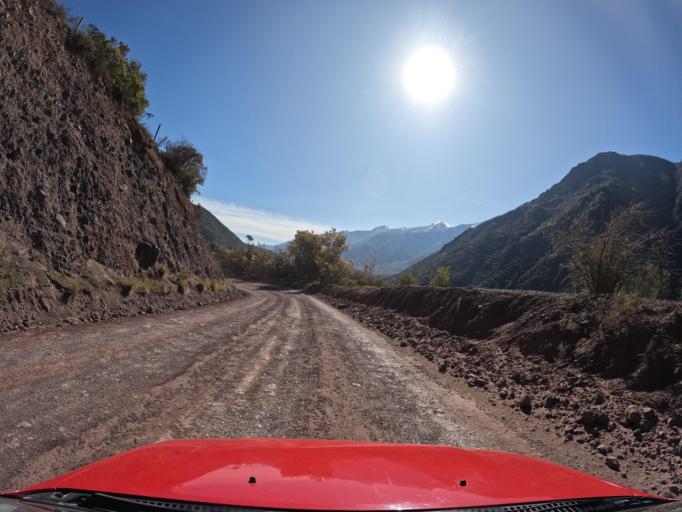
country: CL
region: O'Higgins
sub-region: Provincia de Colchagua
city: Chimbarongo
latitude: -35.0109
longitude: -70.7440
